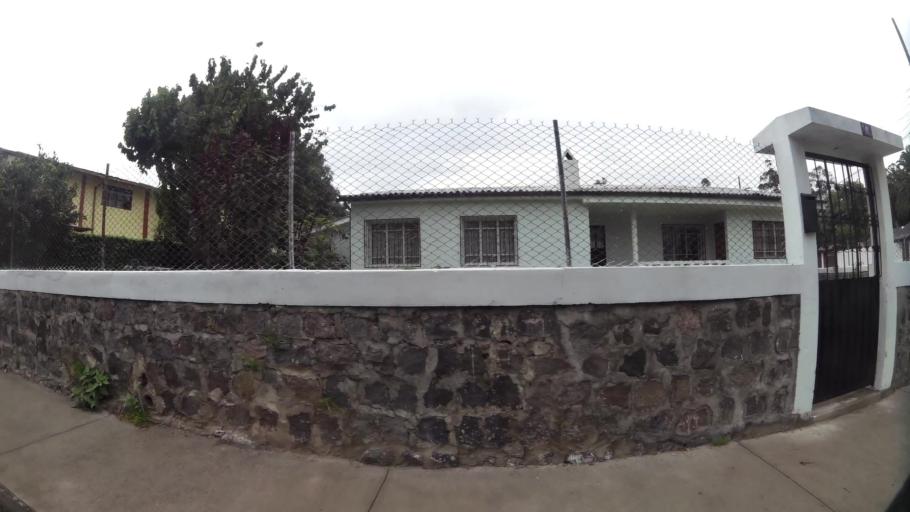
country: EC
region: Pichincha
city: Sangolqui
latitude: -0.3033
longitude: -78.4613
